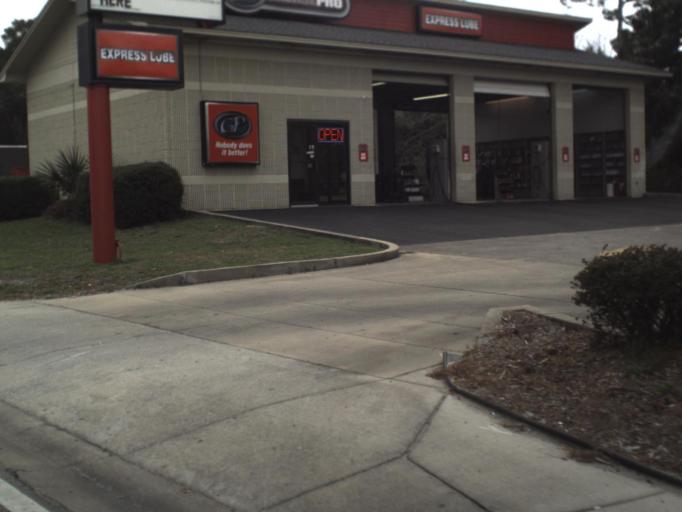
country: US
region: Florida
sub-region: Bay County
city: Pretty Bayou
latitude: 30.1753
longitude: -85.6937
